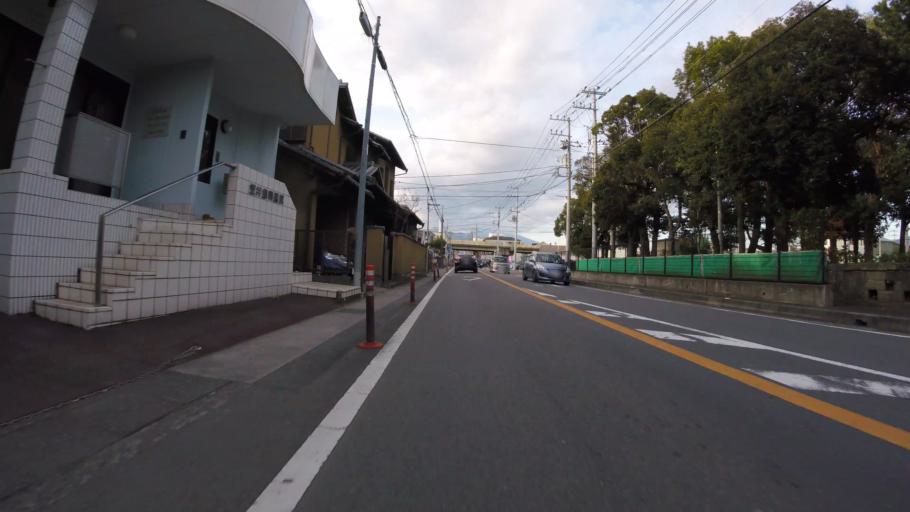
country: JP
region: Shizuoka
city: Mishima
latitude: 35.1123
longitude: 138.9253
